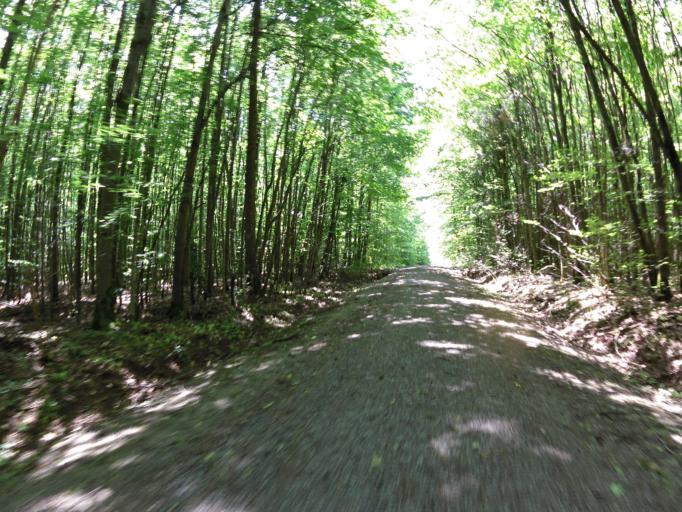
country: DE
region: Bavaria
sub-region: Regierungsbezirk Unterfranken
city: Kist
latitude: 49.7218
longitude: 9.8581
